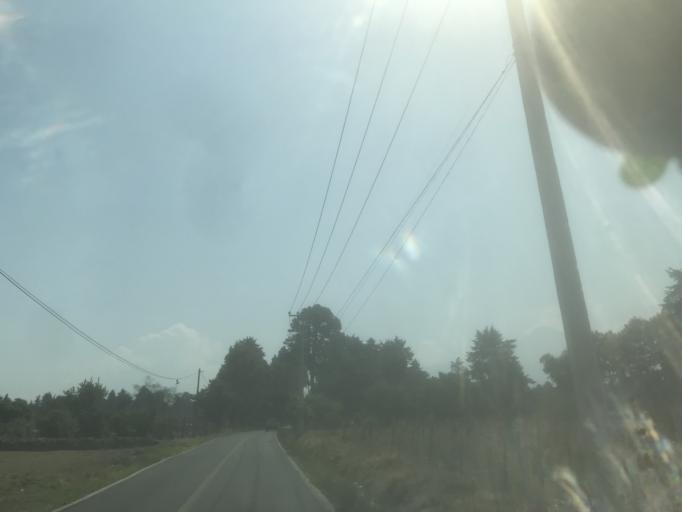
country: MX
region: Mexico
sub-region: Atlautla
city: San Juan Tepecoculco
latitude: 18.9944
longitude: -98.7861
